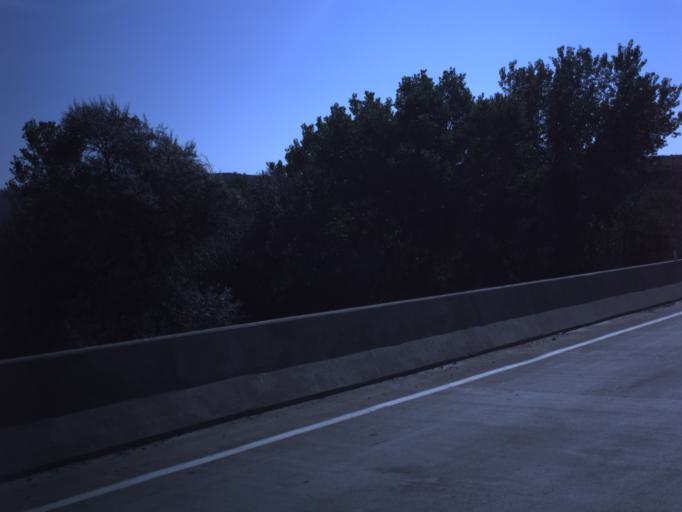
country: US
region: Utah
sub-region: San Juan County
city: Blanding
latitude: 37.2577
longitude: -109.6187
